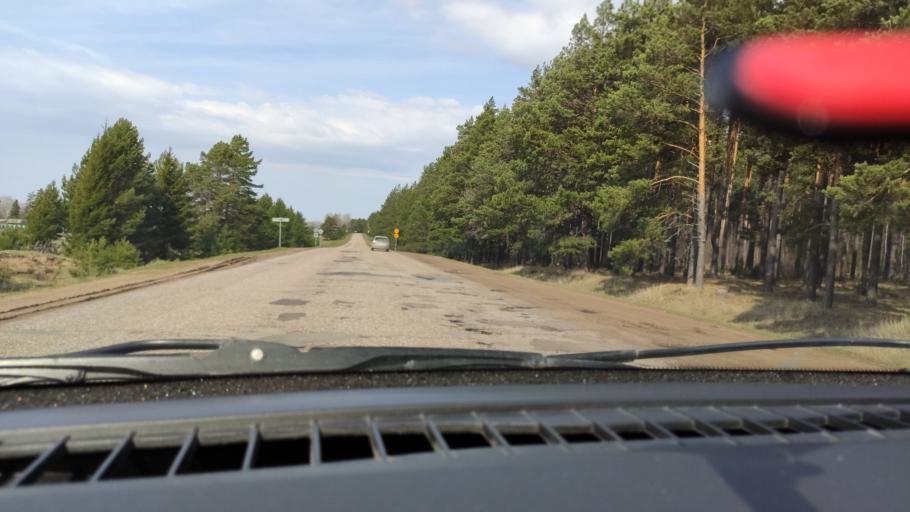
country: RU
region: Bashkortostan
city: Dyurtyuli
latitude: 55.5076
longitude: 54.8923
